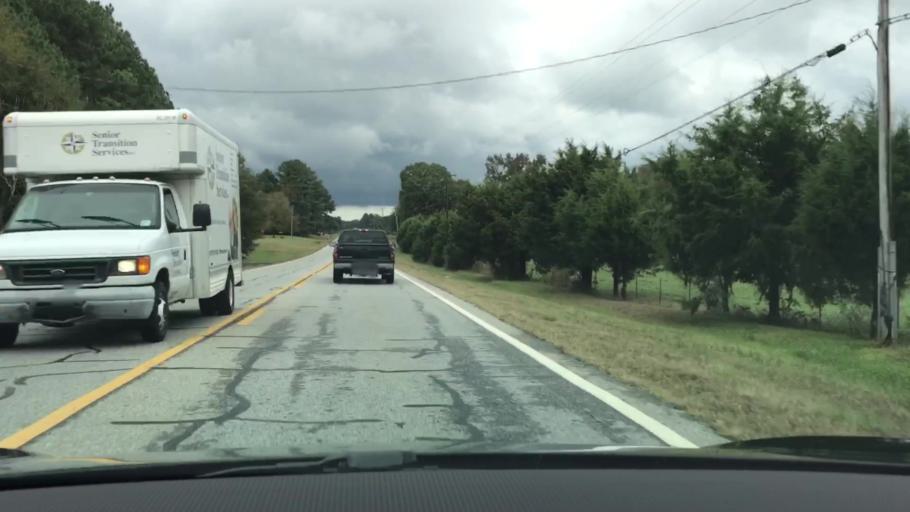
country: US
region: Georgia
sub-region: Oconee County
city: Watkinsville
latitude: 33.7978
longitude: -83.3330
